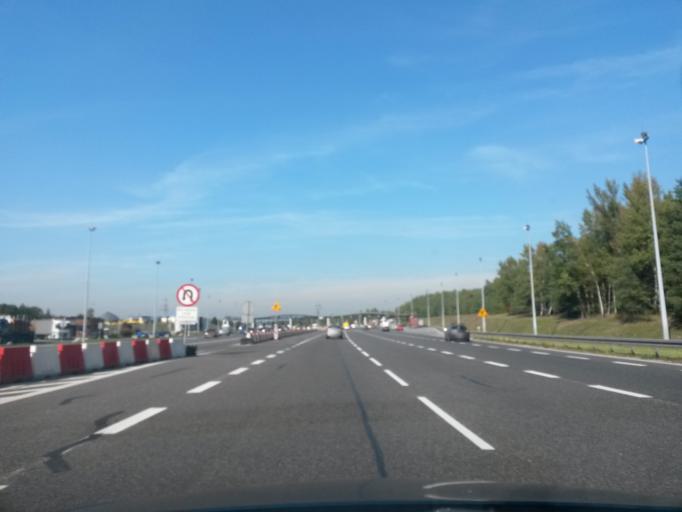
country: PL
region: Silesian Voivodeship
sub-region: Myslowice
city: Myslowice
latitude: 50.1943
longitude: 19.1872
